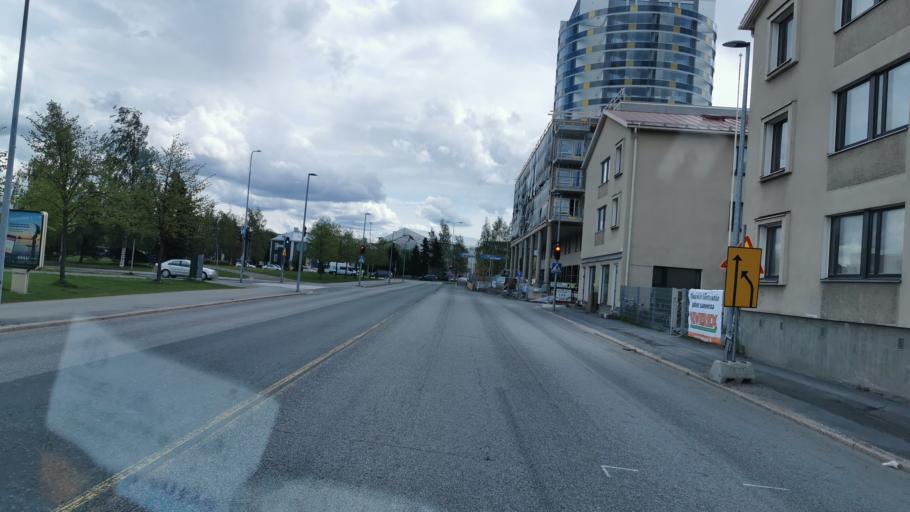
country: FI
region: Northern Ostrobothnia
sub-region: Oulu
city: Oulu
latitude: 65.0046
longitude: 25.4608
